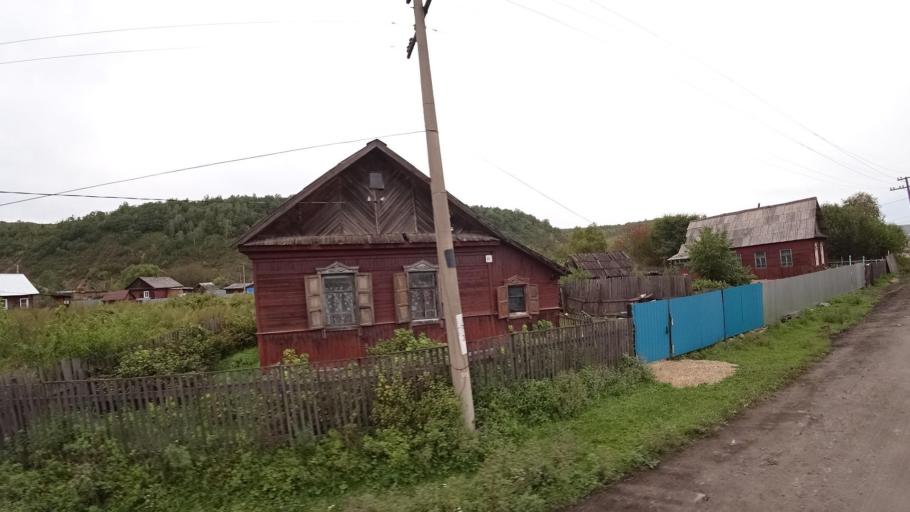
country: RU
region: Jewish Autonomous Oblast
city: Khingansk
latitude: 49.0197
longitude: 131.0486
